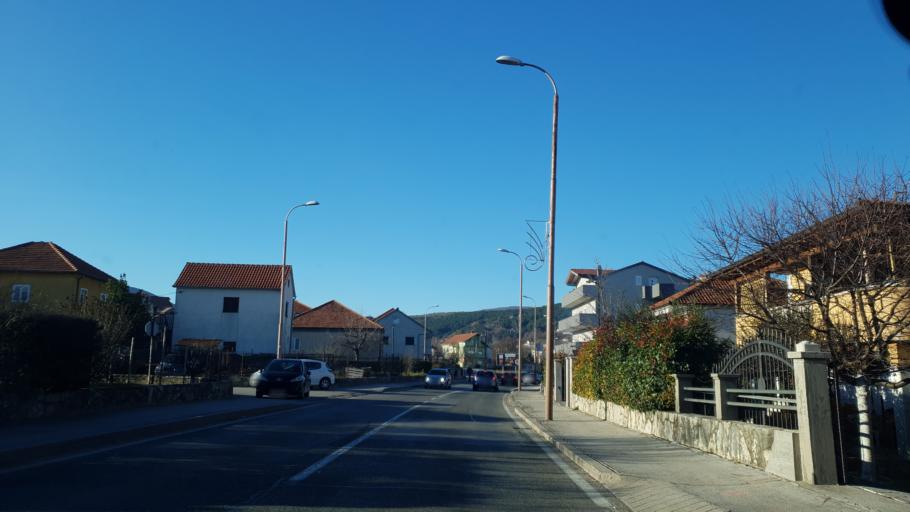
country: HR
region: Splitsko-Dalmatinska
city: Sinj
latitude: 43.6954
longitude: 16.6394
